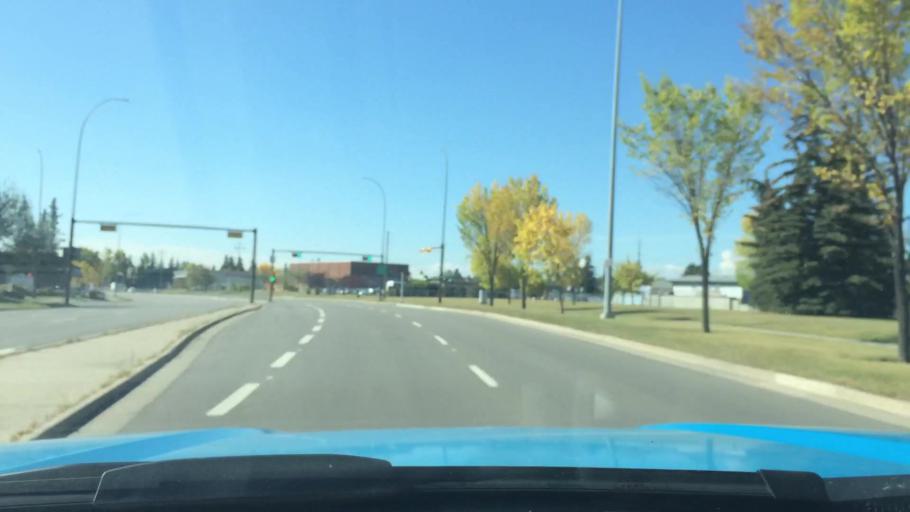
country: CA
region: Alberta
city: Calgary
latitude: 51.1135
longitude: -114.0562
